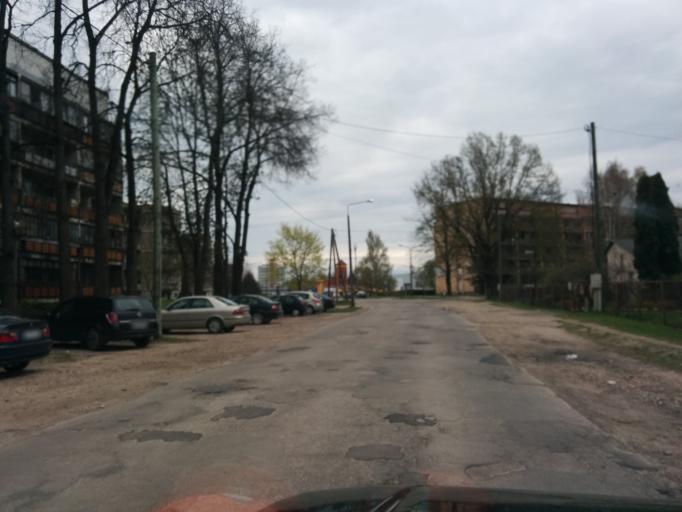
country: LV
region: Ozolnieku
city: Ozolnieki
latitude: 56.6669
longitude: 23.7605
